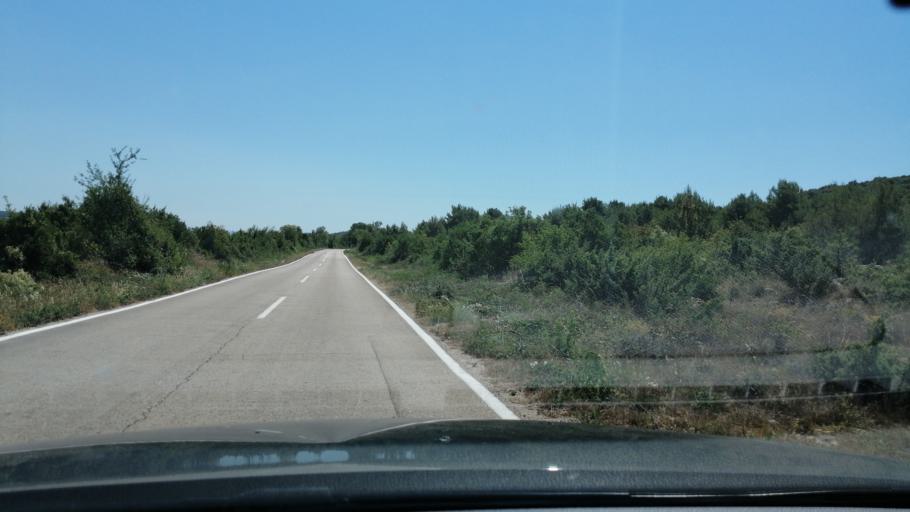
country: HR
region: Sibensko-Kniniska
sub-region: Grad Sibenik
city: Pirovac
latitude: 43.8670
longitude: 15.6854
